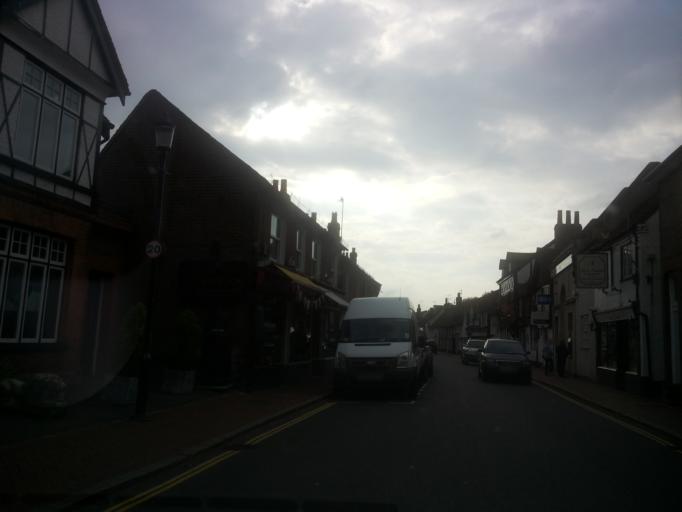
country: GB
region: England
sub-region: Buckinghamshire
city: Great Missenden
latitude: 51.7035
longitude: -0.7072
